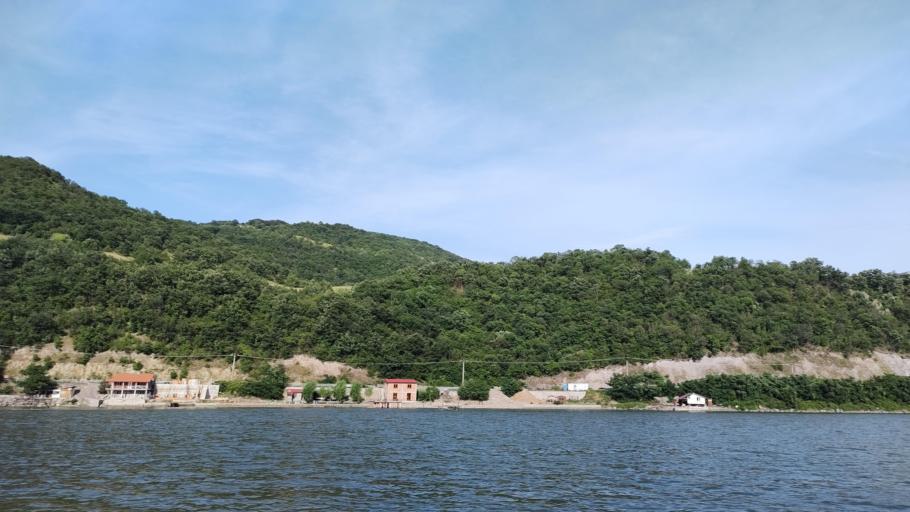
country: RO
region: Mehedinti
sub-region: Comuna Svinita
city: Svinita
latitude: 44.5534
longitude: 22.0339
